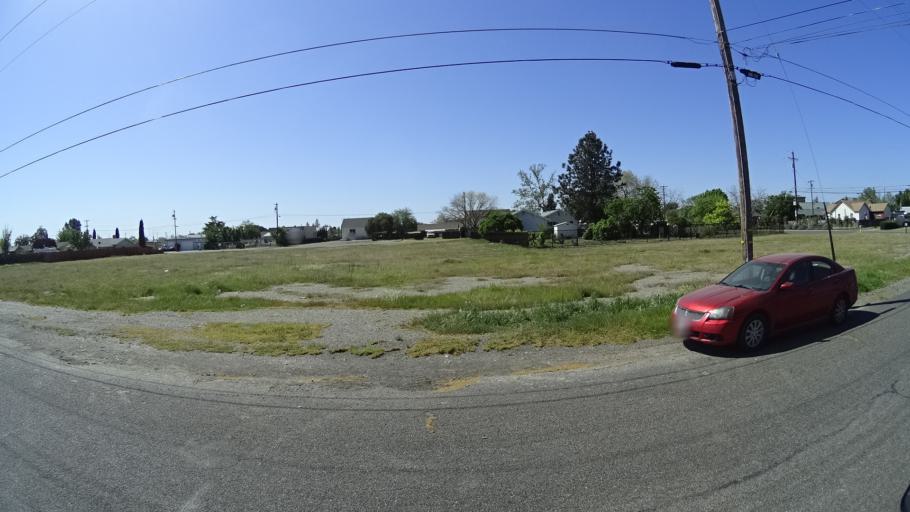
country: US
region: California
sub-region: Glenn County
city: Orland
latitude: 39.7492
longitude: -122.1815
